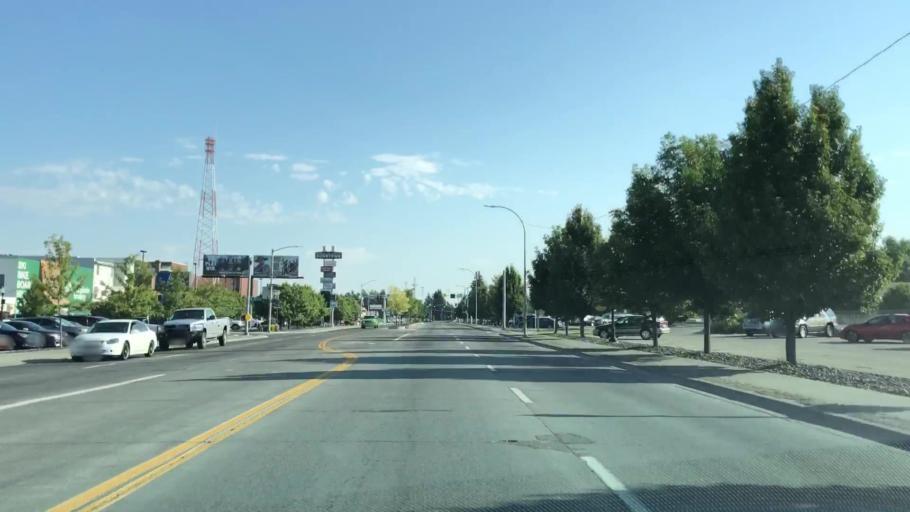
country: US
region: Idaho
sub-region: Bonneville County
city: Idaho Falls
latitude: 43.4910
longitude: -112.0389
